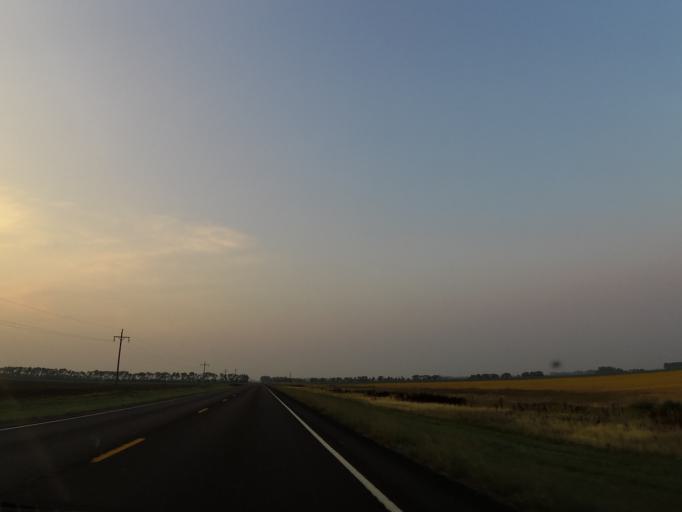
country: US
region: North Dakota
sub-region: Walsh County
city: Park River
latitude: 48.3498
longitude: -97.6223
